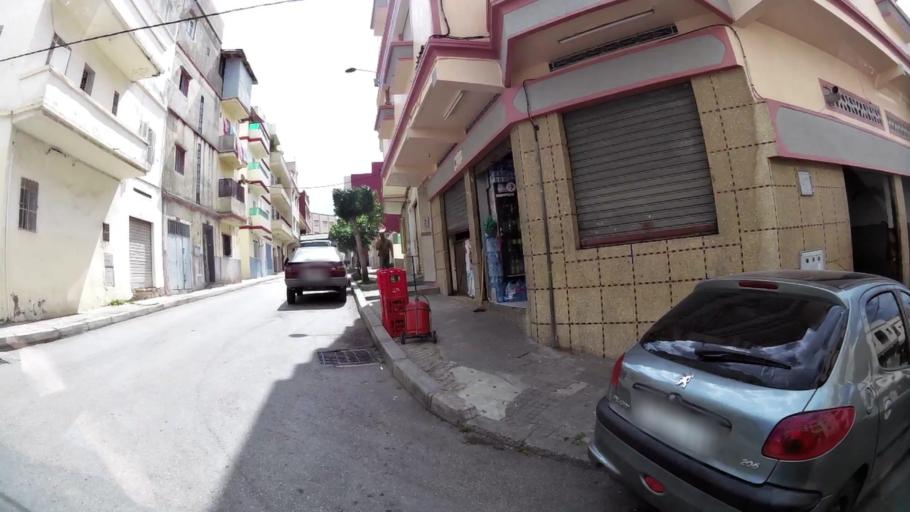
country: MA
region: Tanger-Tetouan
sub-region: Tanger-Assilah
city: Tangier
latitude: 35.7585
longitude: -5.8165
